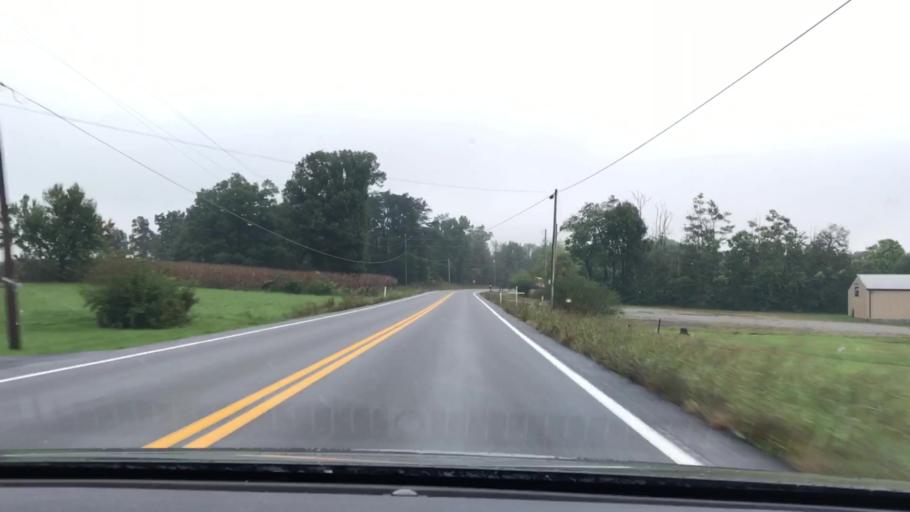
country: US
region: Tennessee
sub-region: Fentress County
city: Grimsley
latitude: 36.1851
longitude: -85.0313
